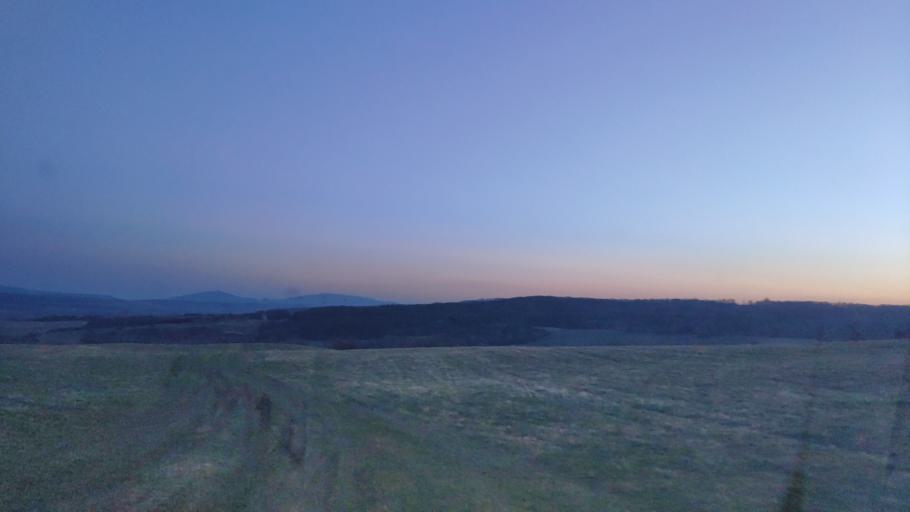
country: SK
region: Kosicky
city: Kosice
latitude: 48.8292
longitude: 21.2614
